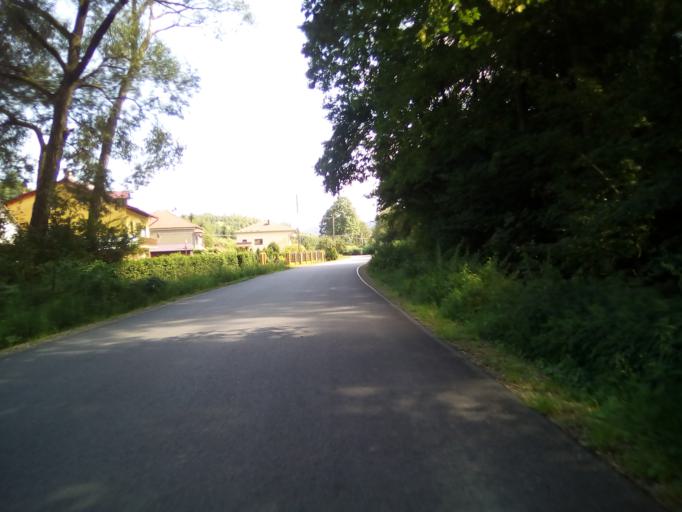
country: PL
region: Subcarpathian Voivodeship
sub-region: Powiat brzozowski
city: Domaradz
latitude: 49.8099
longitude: 21.9265
